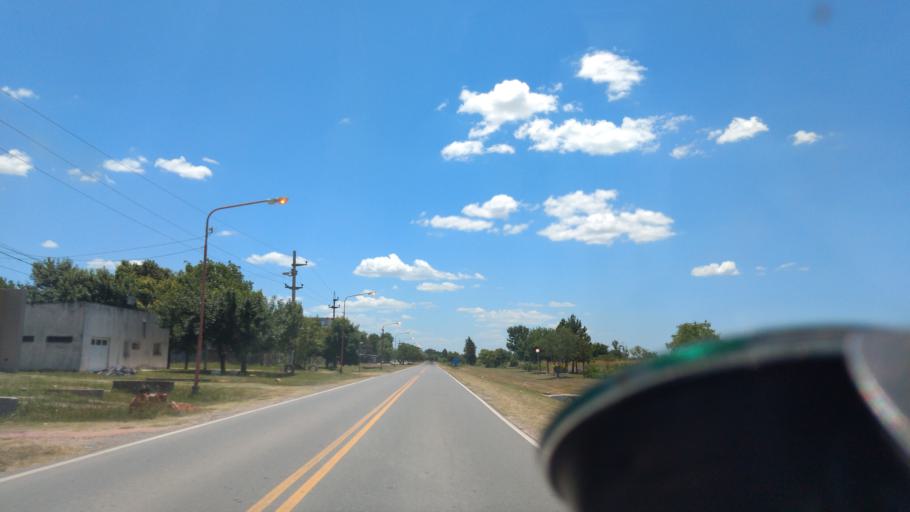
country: AR
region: Santa Fe
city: Laguna Paiva
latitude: -31.3213
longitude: -60.6588
